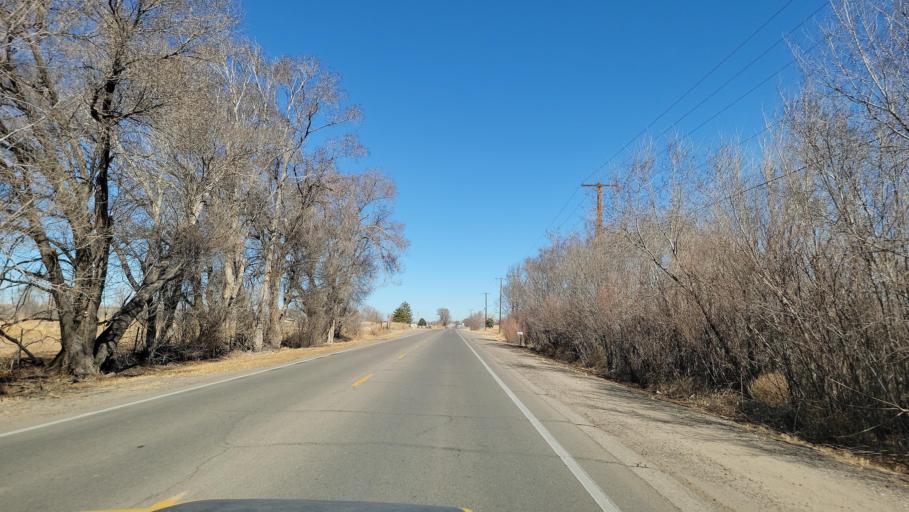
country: US
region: New Mexico
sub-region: Valencia County
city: Bosque Farms
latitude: 34.9274
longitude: -106.6927
